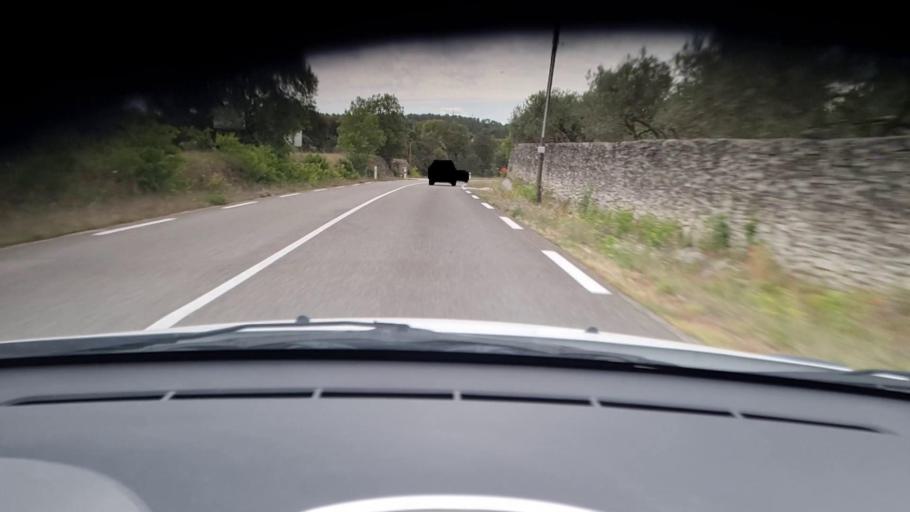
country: FR
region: Languedoc-Roussillon
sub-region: Departement du Gard
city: Uzes
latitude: 43.9858
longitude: 4.4140
